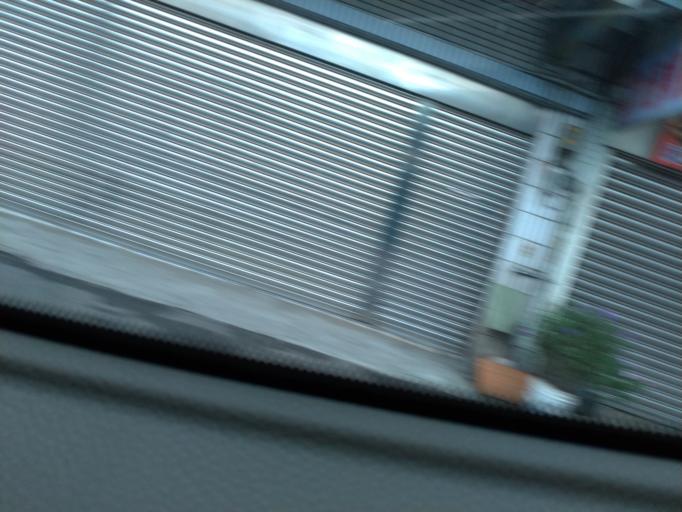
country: TW
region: Taiwan
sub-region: Taoyuan
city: Taoyuan
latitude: 24.9355
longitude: 121.3964
